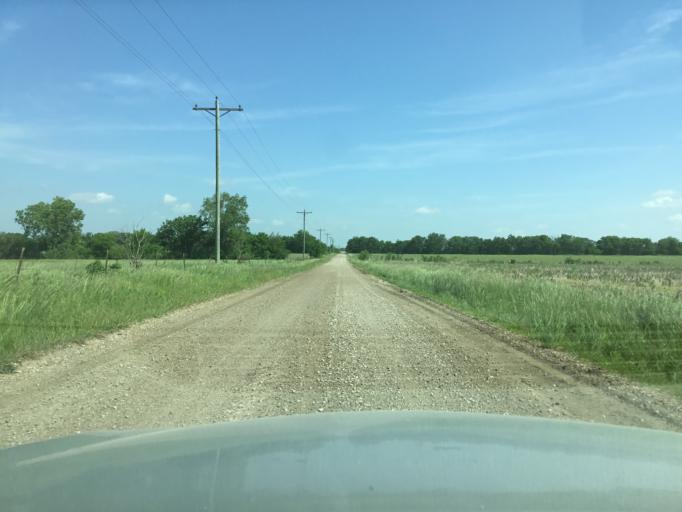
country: US
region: Kansas
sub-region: Labette County
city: Oswego
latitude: 37.1668
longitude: -95.1399
